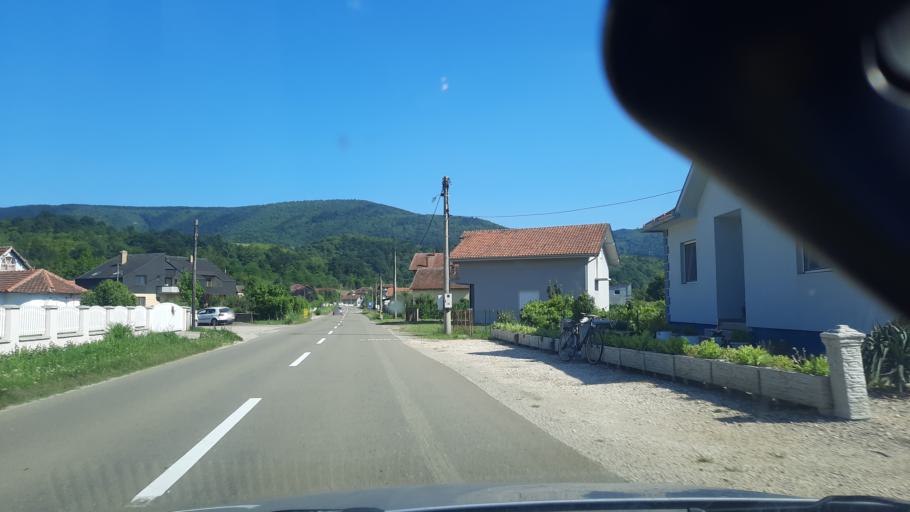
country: RS
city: Turija
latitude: 44.5253
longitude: 21.6369
